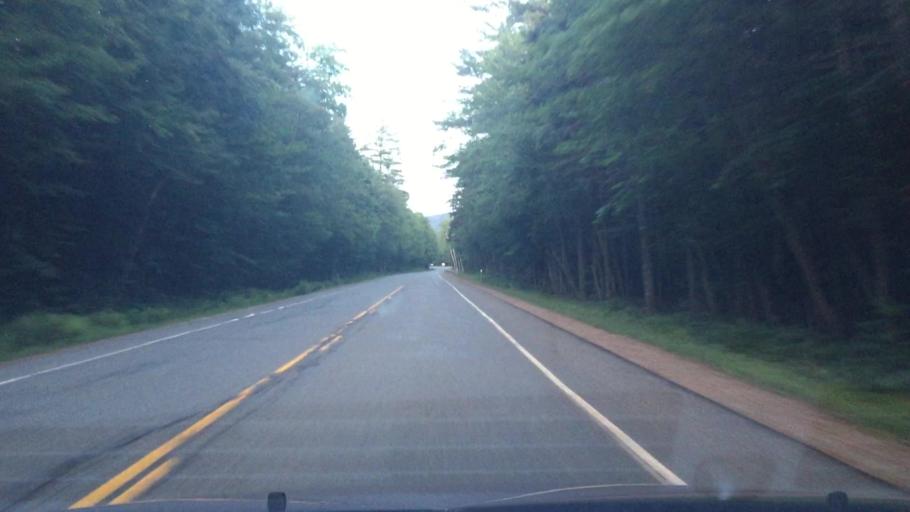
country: US
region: New Hampshire
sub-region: Grafton County
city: Woodstock
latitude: 44.0418
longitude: -71.5493
